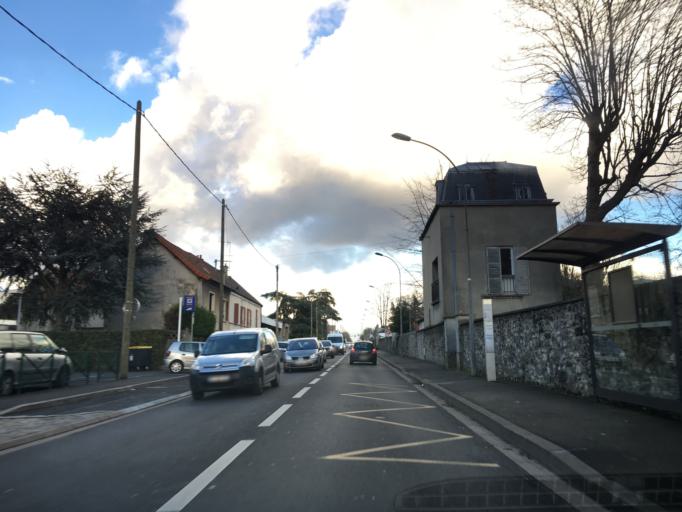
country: FR
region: Ile-de-France
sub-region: Departement du Val-de-Marne
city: Ormesson-sur-Marne
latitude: 48.7862
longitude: 2.5414
